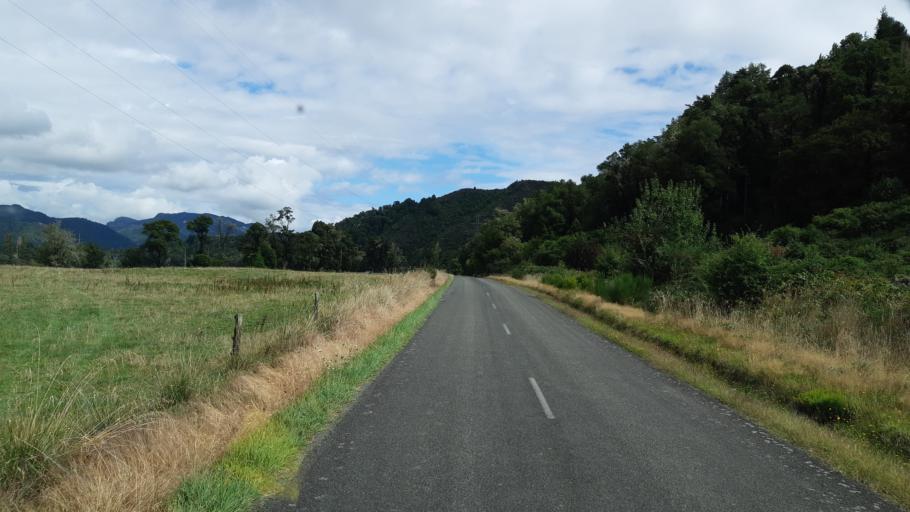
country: NZ
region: West Coast
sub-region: Buller District
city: Westport
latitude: -41.7895
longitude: 172.3640
